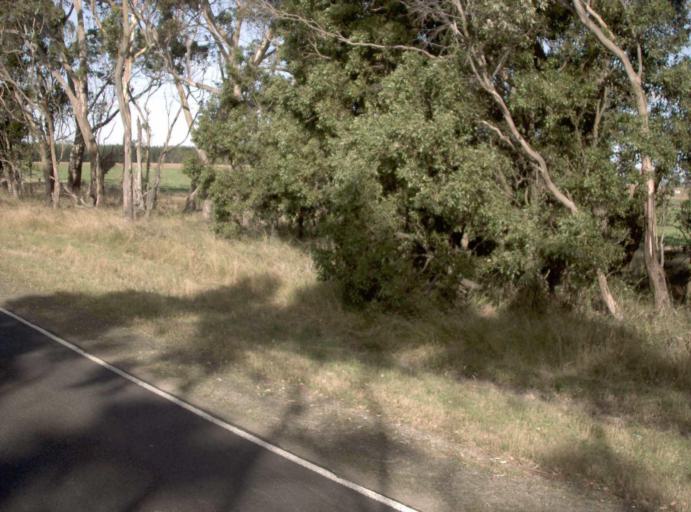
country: AU
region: Victoria
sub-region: Latrobe
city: Traralgon
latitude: -38.2354
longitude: 146.5112
